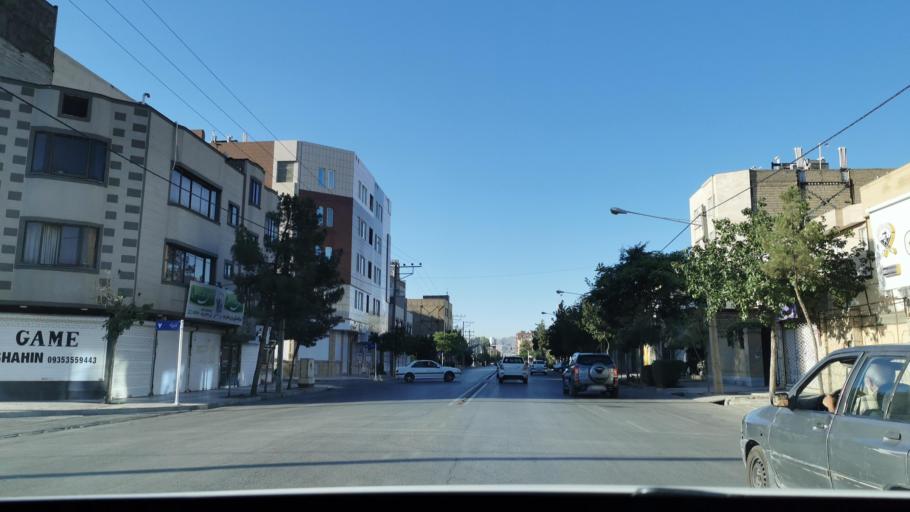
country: IR
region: Razavi Khorasan
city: Mashhad
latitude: 36.3541
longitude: 59.4973
